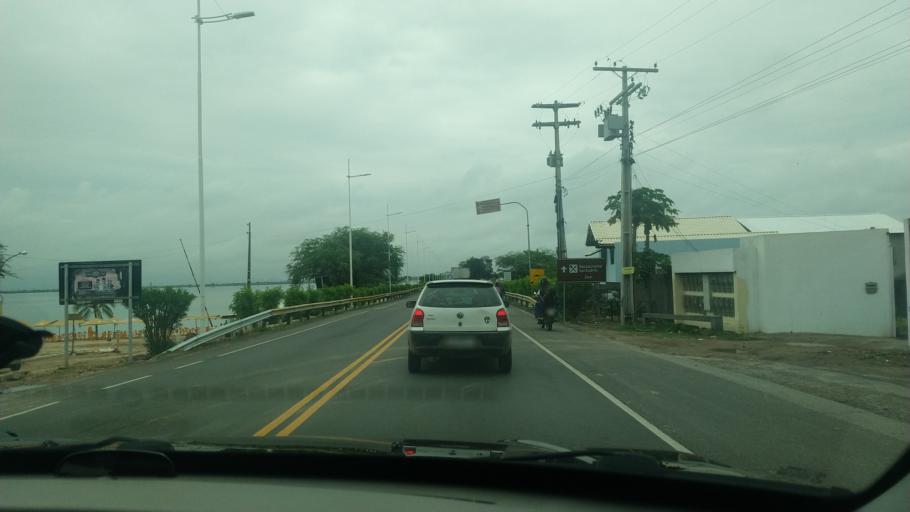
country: BR
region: Bahia
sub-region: Paulo Afonso
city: Paulo Afonso
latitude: -9.4109
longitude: -38.2356
